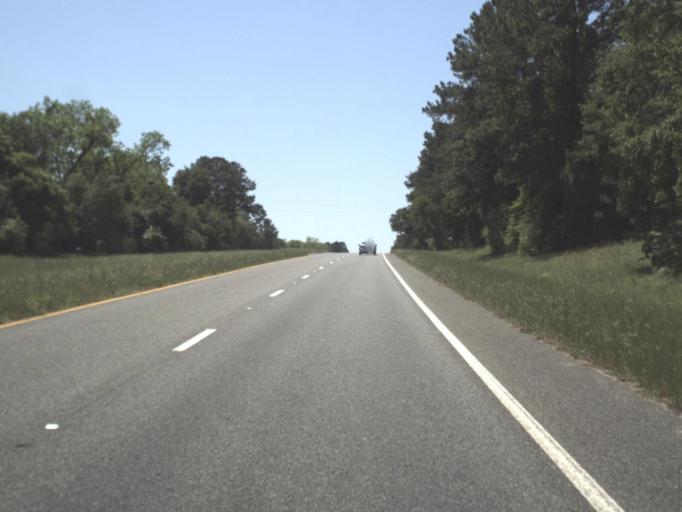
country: US
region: Florida
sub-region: Jefferson County
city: Monticello
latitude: 30.5737
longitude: -83.8701
